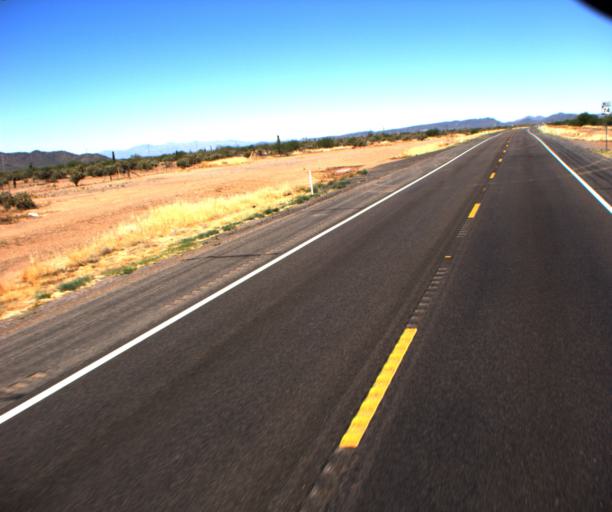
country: US
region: Arizona
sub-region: Maricopa County
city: Anthem
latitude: 33.7979
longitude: -112.1834
